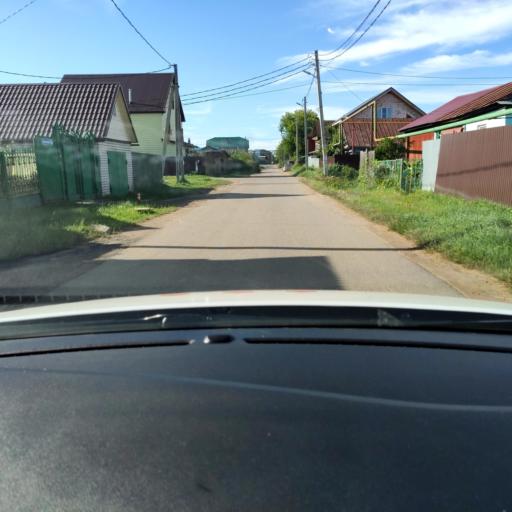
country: RU
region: Tatarstan
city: Verkhniy Uslon
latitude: 55.8018
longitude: 49.0327
